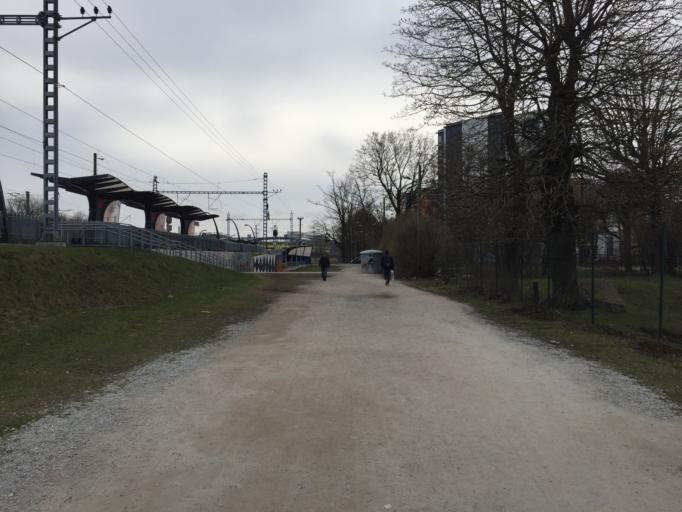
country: EE
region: Harju
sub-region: Tallinna linn
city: Tallinn
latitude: 59.4256
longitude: 24.7271
